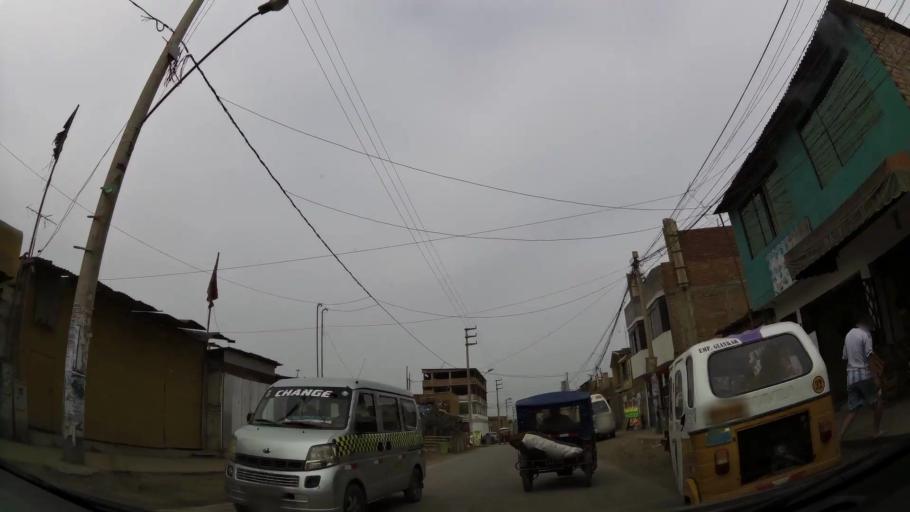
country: PE
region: Lima
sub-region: Lima
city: Surco
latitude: -12.2380
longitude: -76.9361
